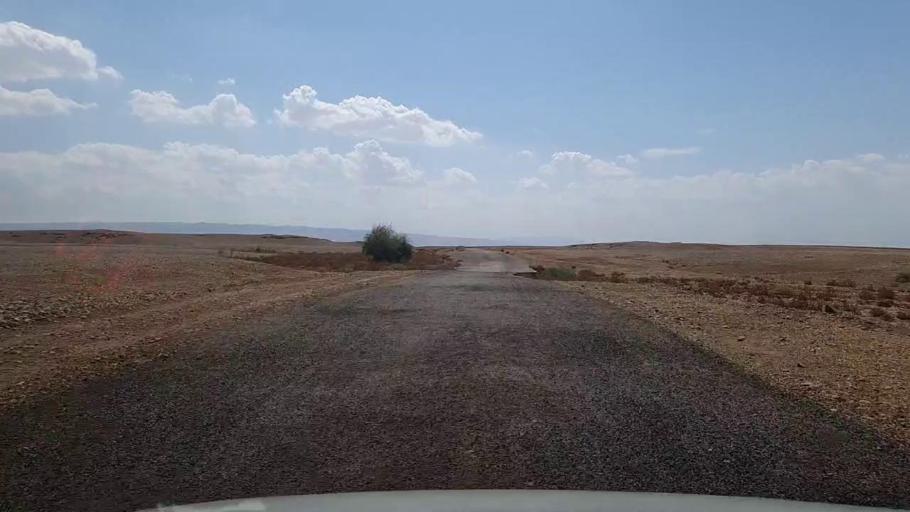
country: PK
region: Sindh
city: Bhan
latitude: 26.3808
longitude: 67.6336
